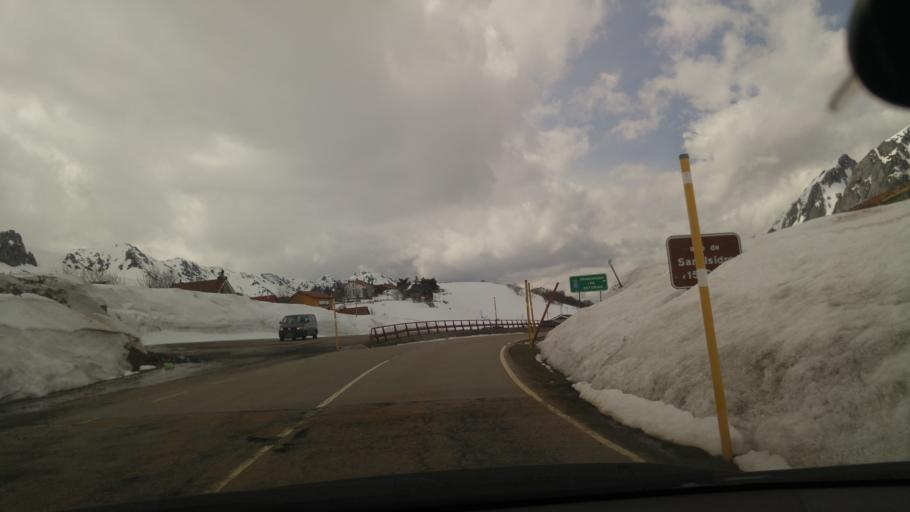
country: ES
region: Asturias
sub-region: Province of Asturias
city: Campo de Caso
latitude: 43.0655
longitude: -5.3861
